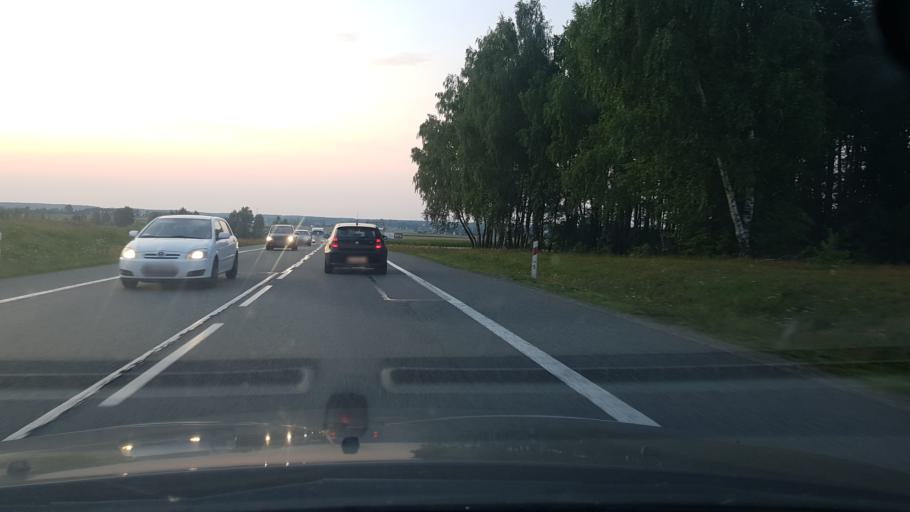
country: PL
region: Masovian Voivodeship
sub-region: Powiat mlawski
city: Wieczfnia Koscielna
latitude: 53.2089
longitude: 20.4326
